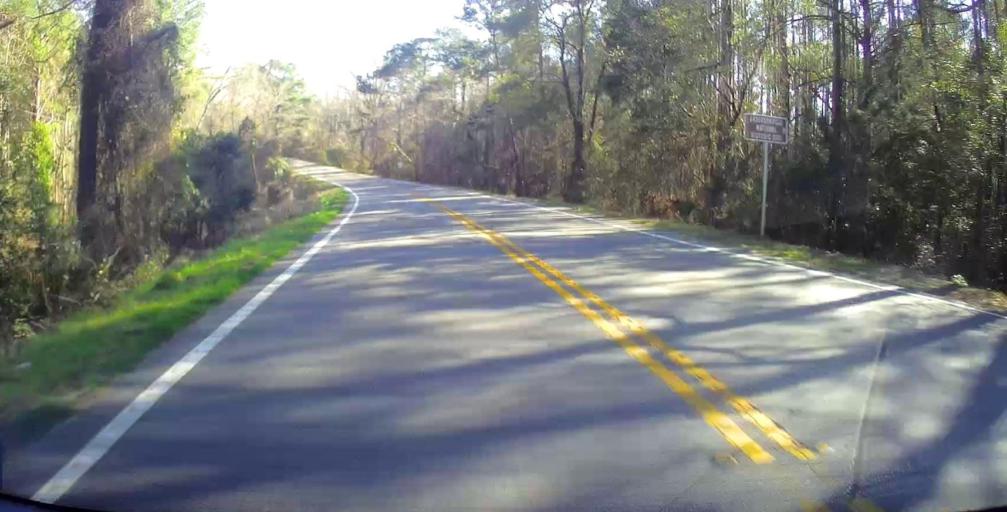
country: US
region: Georgia
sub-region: Macon County
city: Oglethorpe
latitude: 32.3687
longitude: -84.1882
